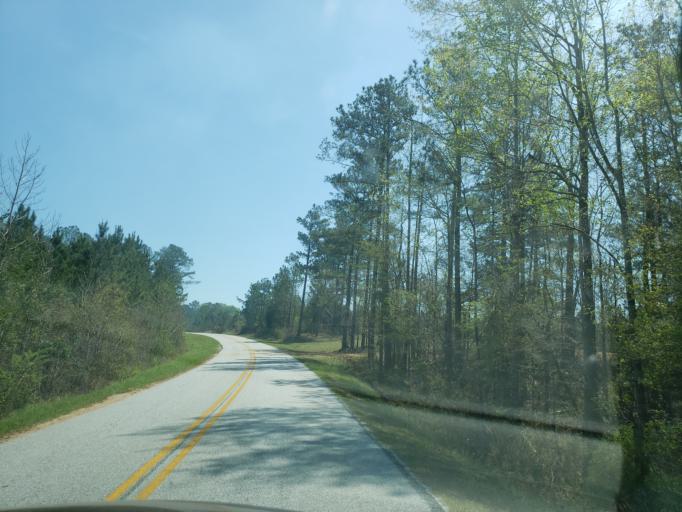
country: US
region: Alabama
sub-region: Elmore County
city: Tallassee
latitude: 32.6676
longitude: -85.8576
